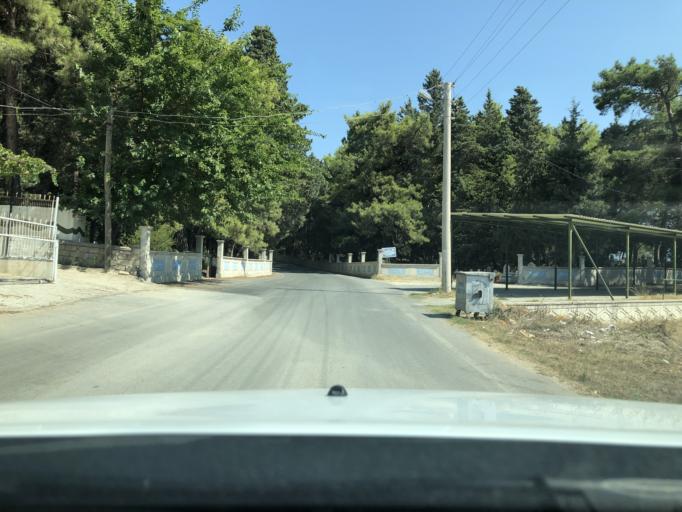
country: TR
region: Antalya
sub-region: Manavgat
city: Manavgat
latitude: 36.8145
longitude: 31.4888
